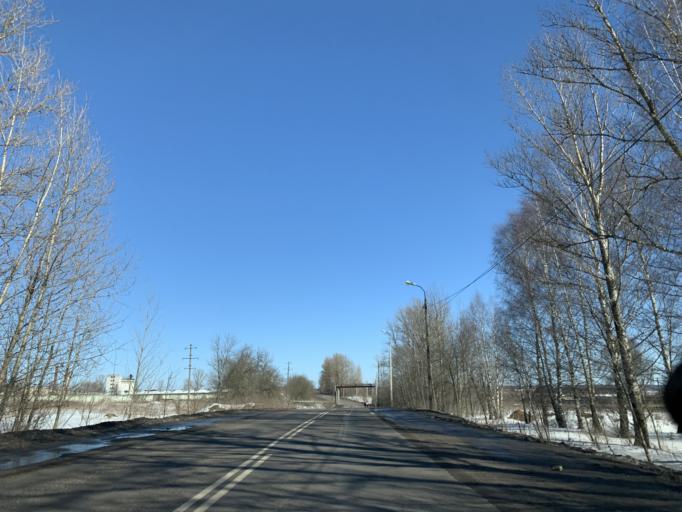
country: RU
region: Jaroslavl
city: Konstantinovskiy
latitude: 57.8353
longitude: 39.5598
